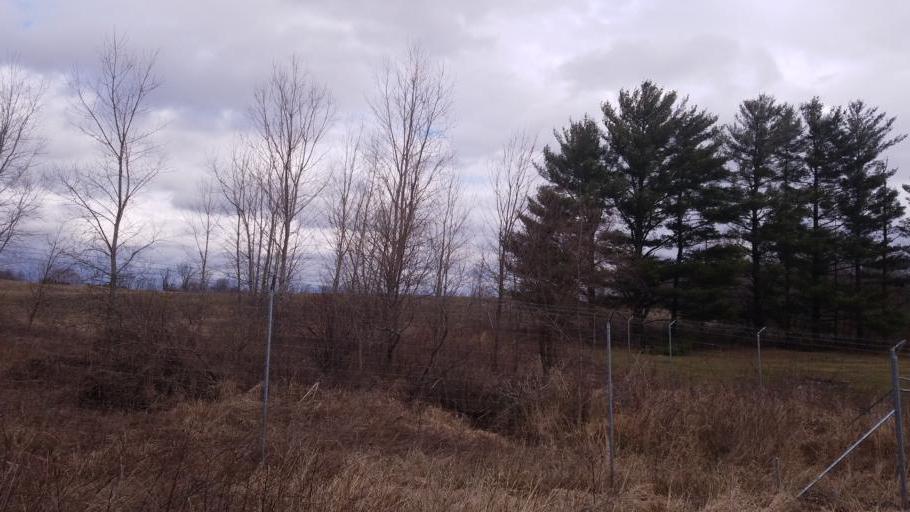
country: US
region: Ohio
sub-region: Knox County
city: Mount Vernon
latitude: 40.3256
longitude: -82.5106
